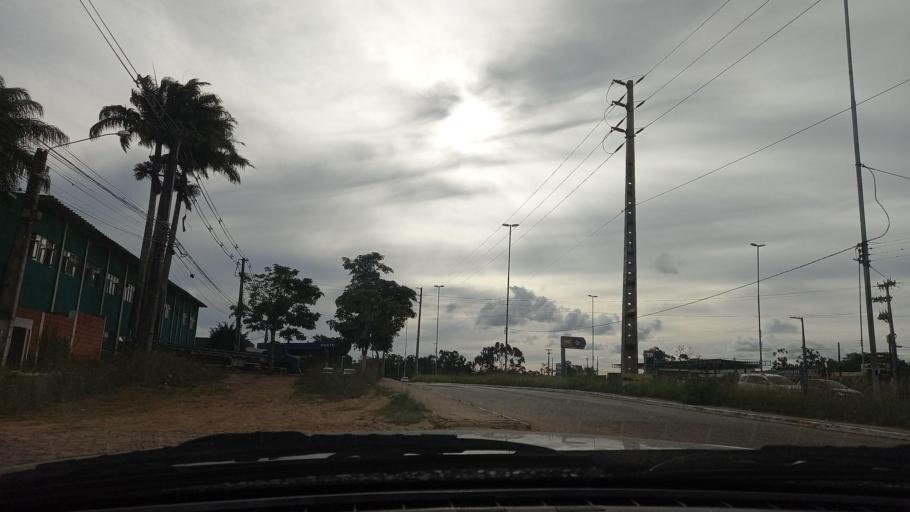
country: BR
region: Pernambuco
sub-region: Gravata
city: Gravata
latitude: -8.1936
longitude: -35.5440
